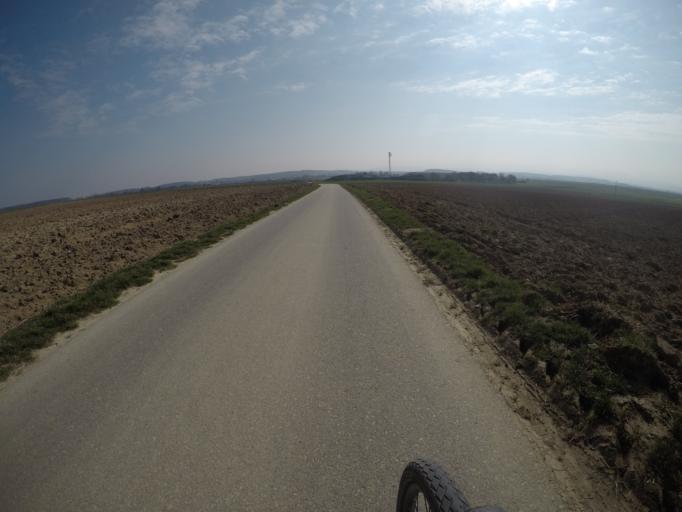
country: DE
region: Baden-Wuerttemberg
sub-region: Regierungsbezirk Stuttgart
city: Wolfschlugen
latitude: 48.6544
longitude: 9.2589
